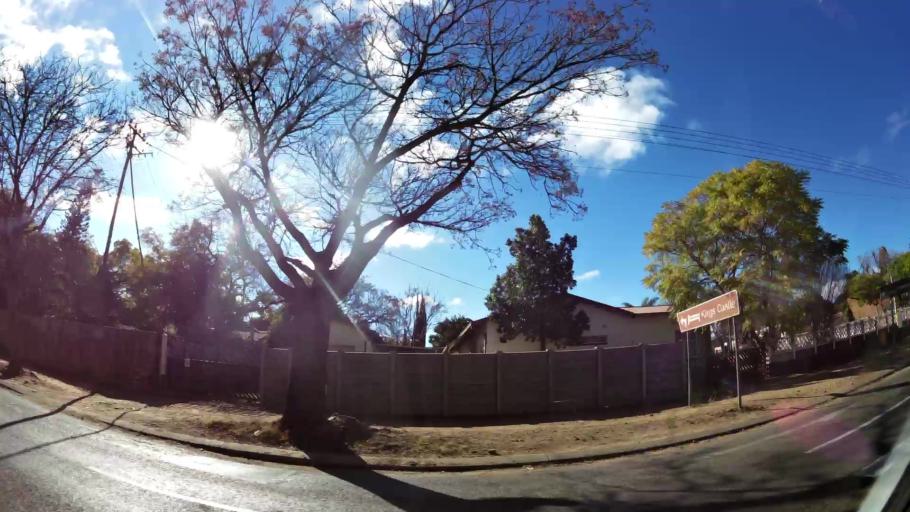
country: ZA
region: Limpopo
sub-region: Capricorn District Municipality
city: Polokwane
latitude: -23.9074
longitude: 29.4595
